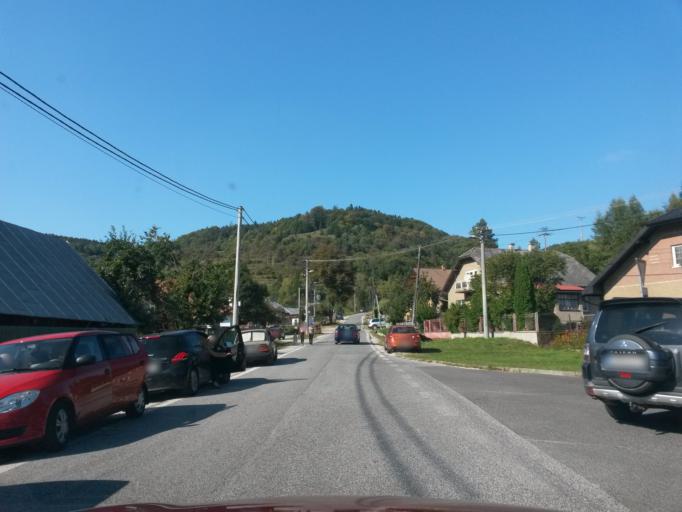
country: SK
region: Kosicky
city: Spisska Nova Ves
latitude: 48.8479
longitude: 20.6118
